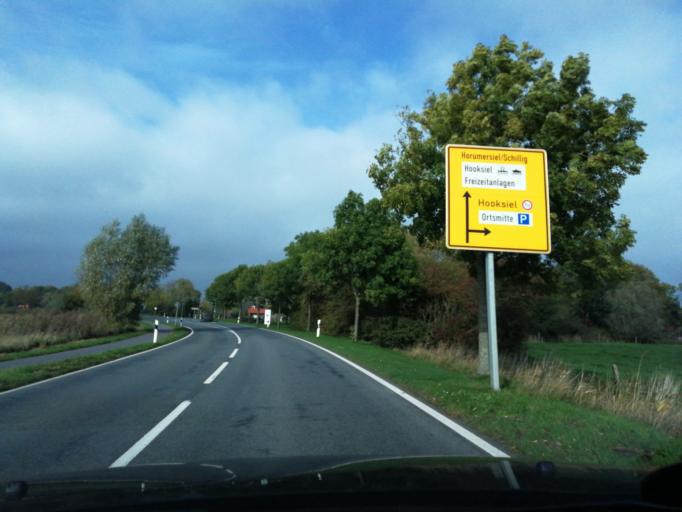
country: DE
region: Lower Saxony
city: Fedderwarden
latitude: 53.6220
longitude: 8.0337
